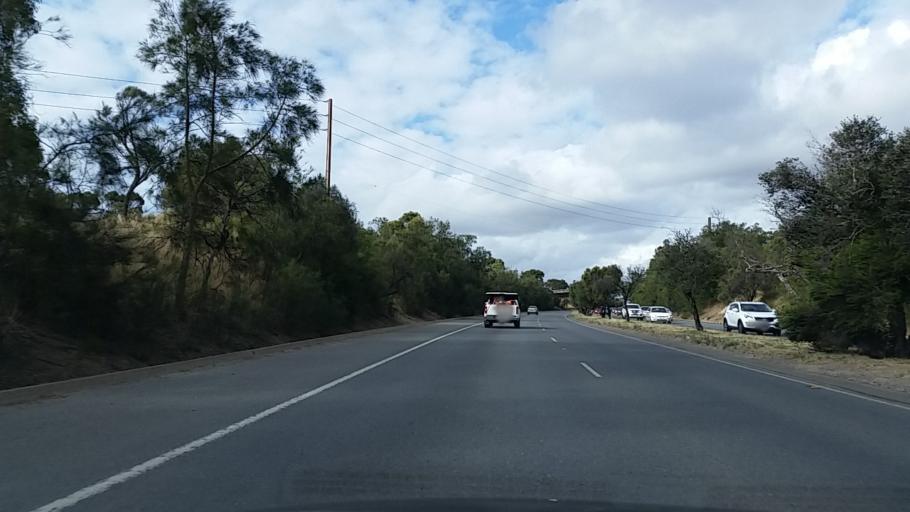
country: AU
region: South Australia
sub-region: Onkaparinga
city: Noarlunga
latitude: -35.1740
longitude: 138.4998
